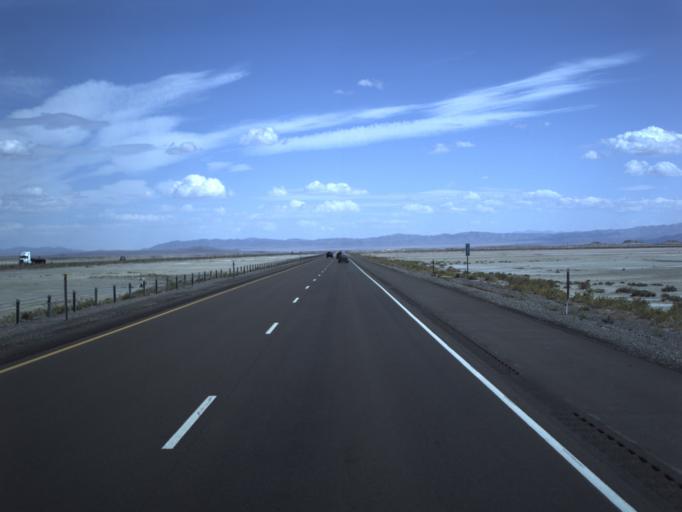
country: US
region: Utah
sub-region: Tooele County
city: Wendover
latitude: 40.7277
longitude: -113.3412
